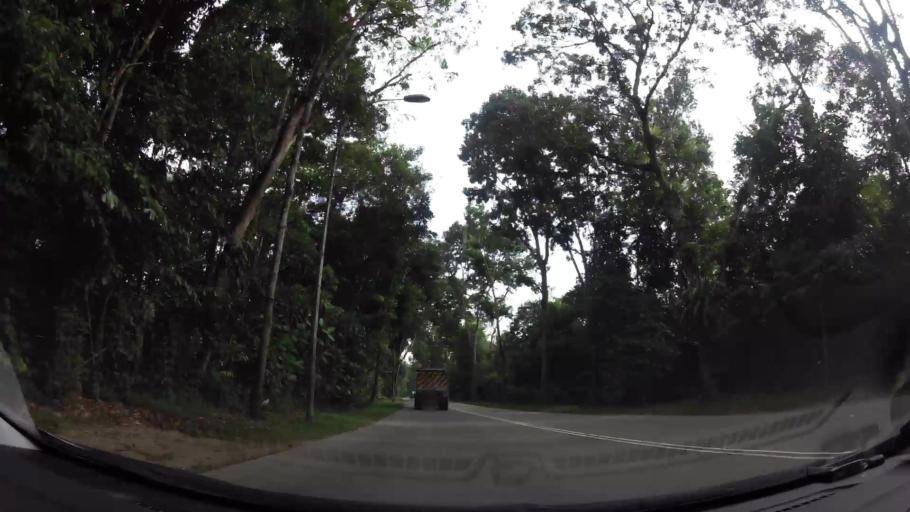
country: MY
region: Johor
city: Johor Bahru
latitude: 1.4120
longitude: 103.6999
